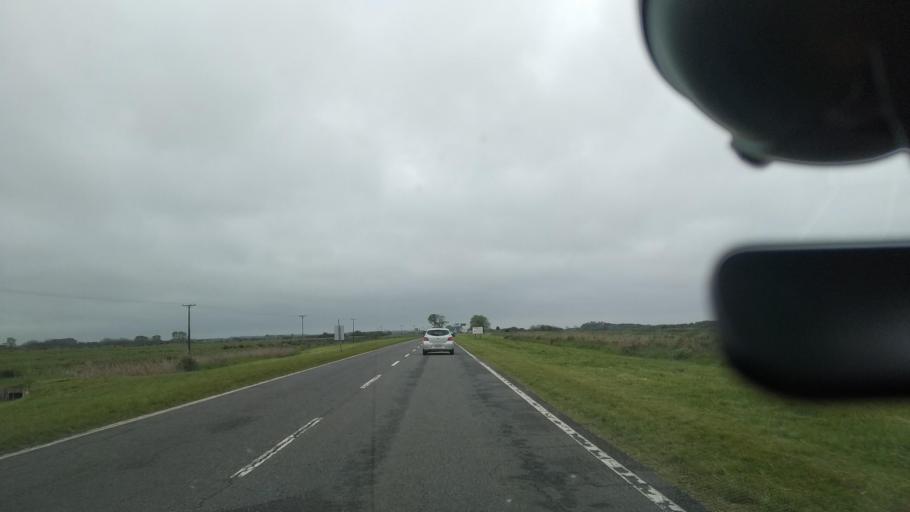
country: AR
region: Buenos Aires
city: Veronica
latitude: -35.5990
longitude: -57.2740
